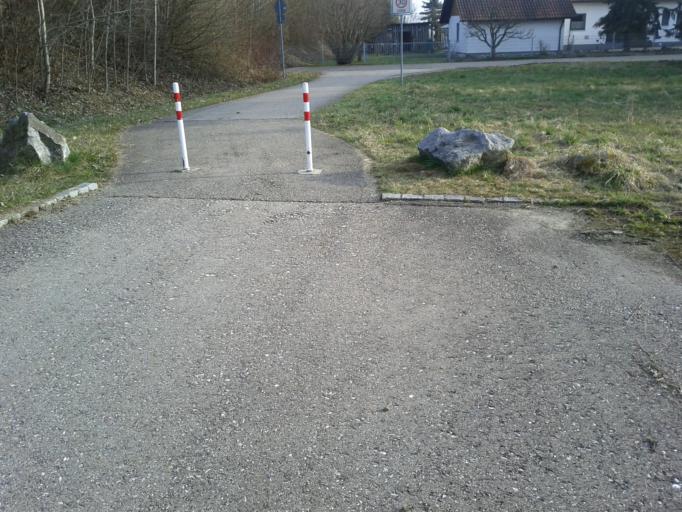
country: DE
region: Bavaria
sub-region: Swabia
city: Guenzburg
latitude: 48.4449
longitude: 10.2891
